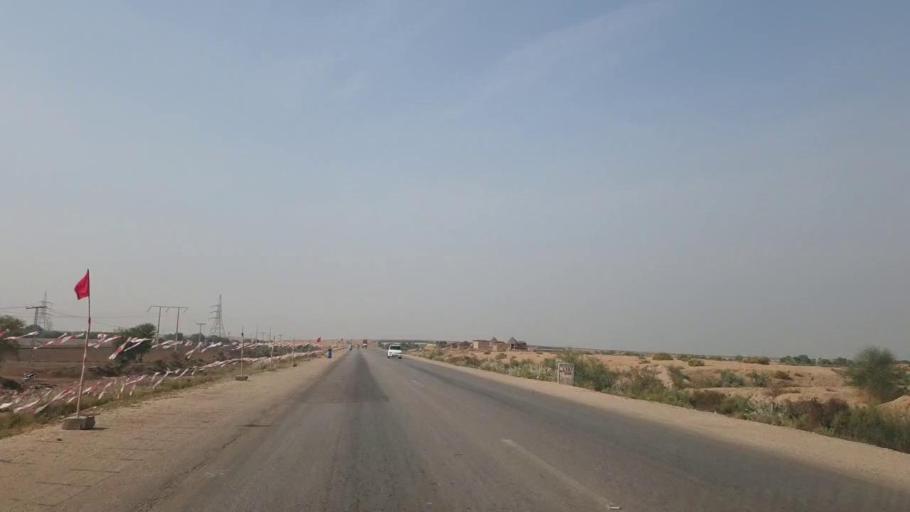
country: PK
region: Sindh
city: Sann
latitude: 26.1507
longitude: 68.0281
